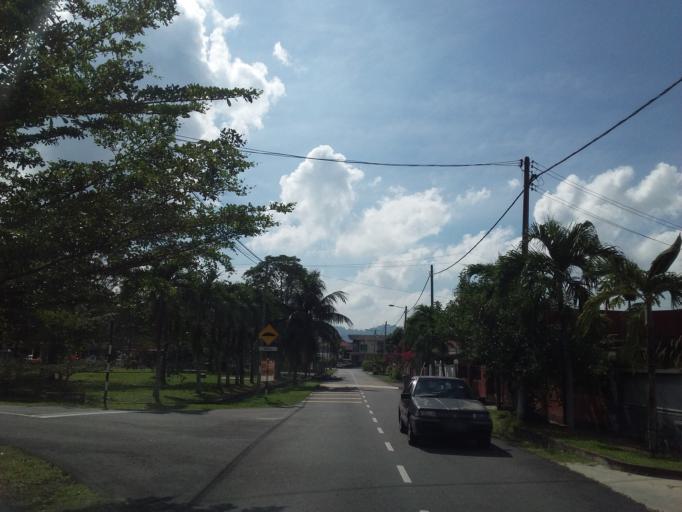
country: MY
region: Johor
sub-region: Daerah Batu Pahat
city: Batu Pahat
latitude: 1.8400
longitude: 102.9282
